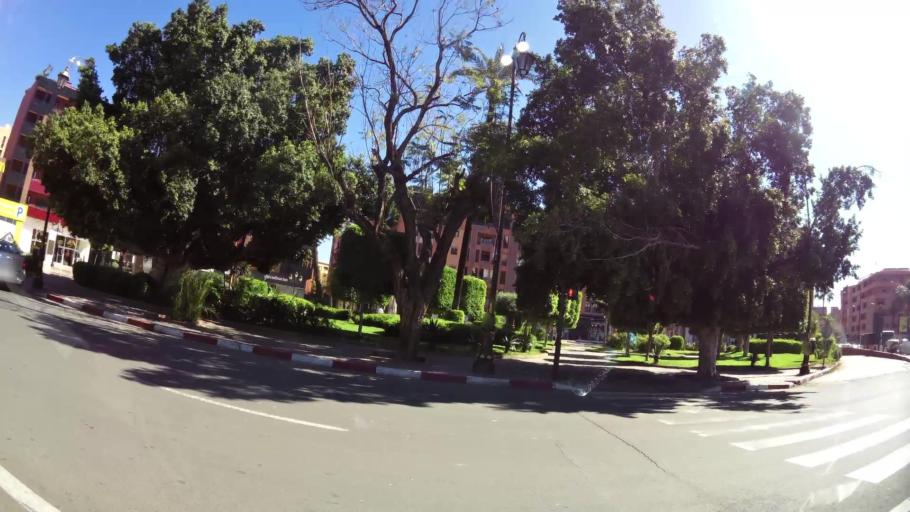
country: MA
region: Marrakech-Tensift-Al Haouz
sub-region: Marrakech
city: Marrakesh
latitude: 31.6326
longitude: -8.0084
